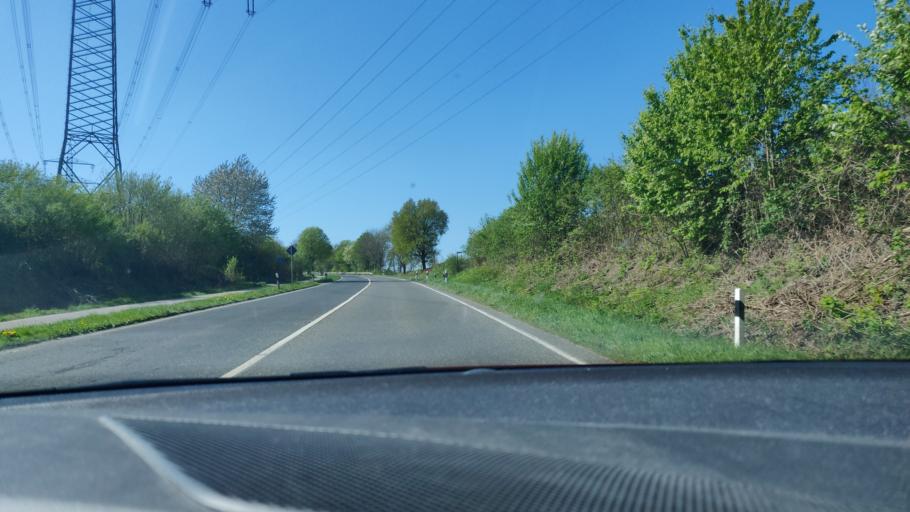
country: DE
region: North Rhine-Westphalia
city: Wulfrath
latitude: 51.3009
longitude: 7.0025
